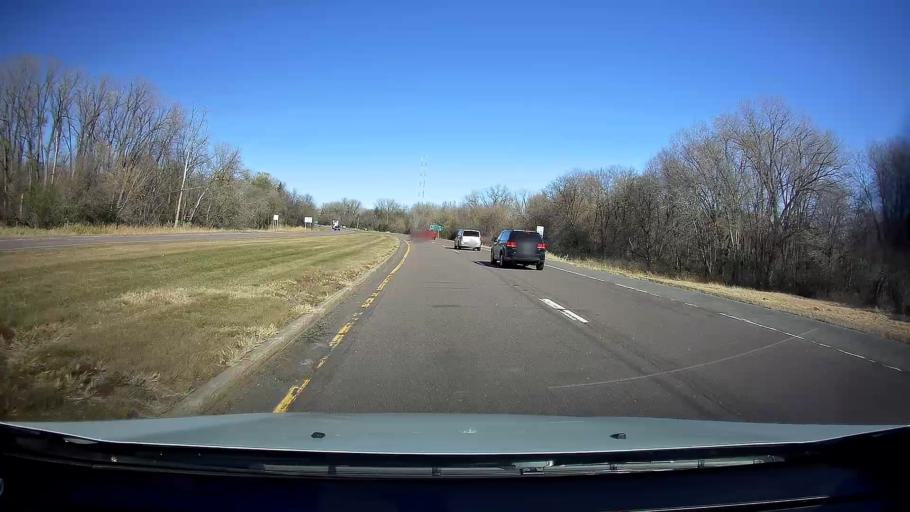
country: US
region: Minnesota
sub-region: Ramsey County
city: Arden Hills
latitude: 45.0387
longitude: -93.1595
